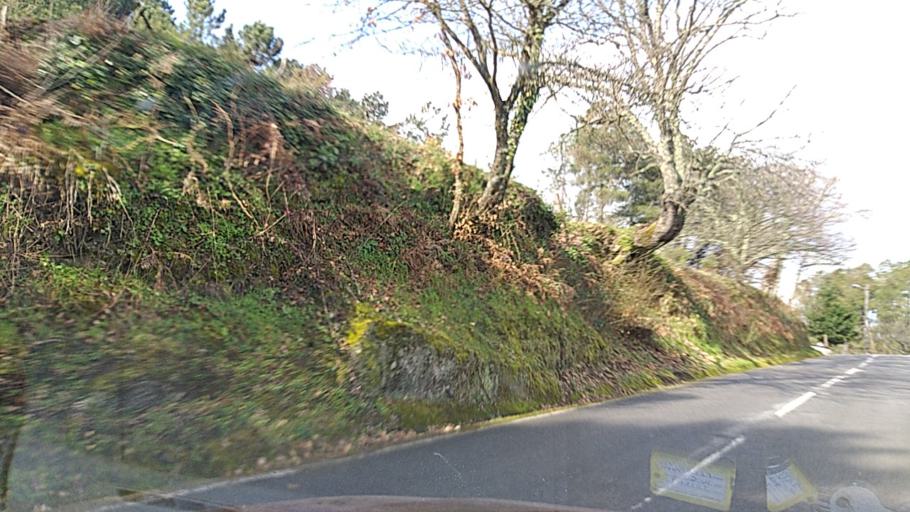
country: PT
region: Guarda
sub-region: Fornos de Algodres
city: Fornos de Algodres
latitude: 40.6599
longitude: -7.6324
